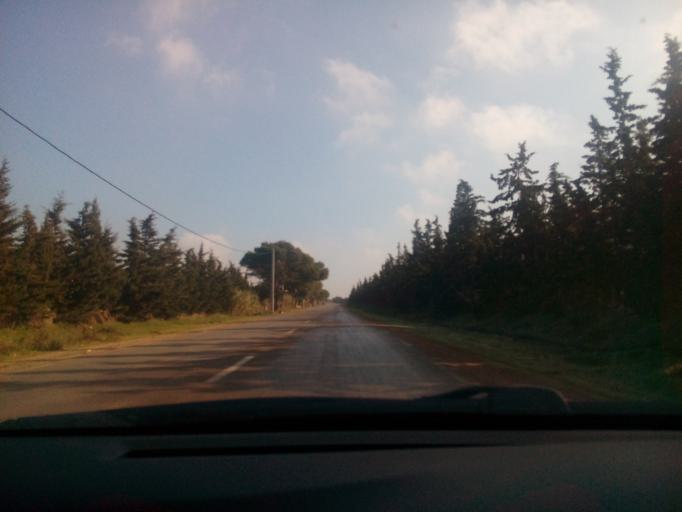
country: DZ
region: Oran
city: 'Ain el Turk
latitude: 35.7037
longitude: -0.8439
